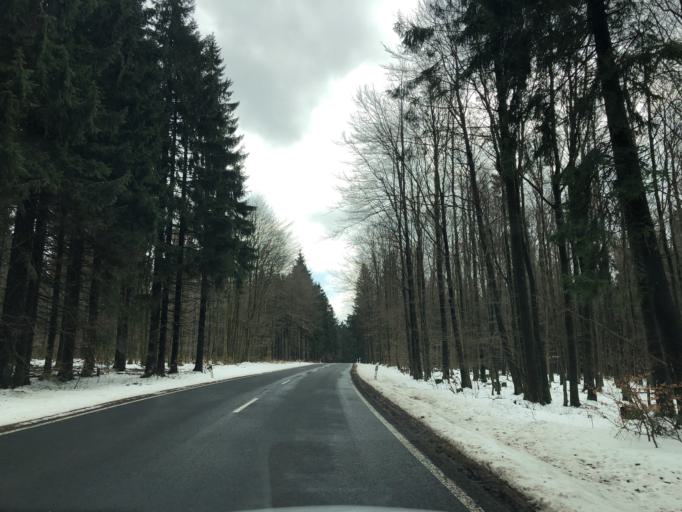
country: DE
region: Hesse
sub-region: Regierungsbezirk Giessen
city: Ulrichstein
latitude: 50.5382
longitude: 9.2200
